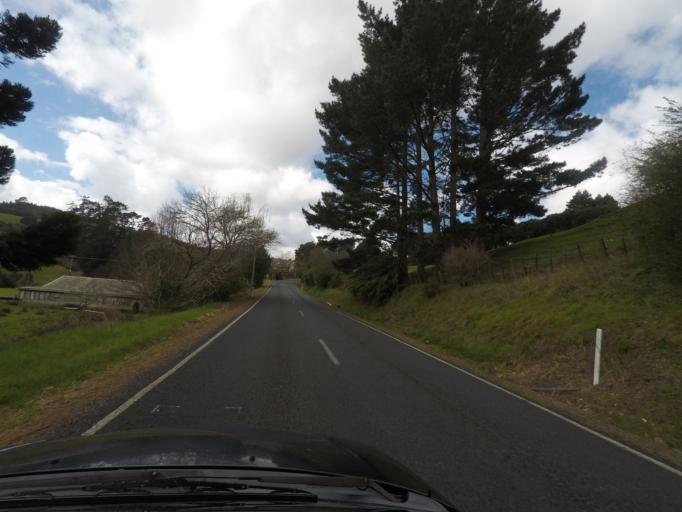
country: NZ
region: Auckland
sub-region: Auckland
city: Red Hill
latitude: -37.1153
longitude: 175.1049
